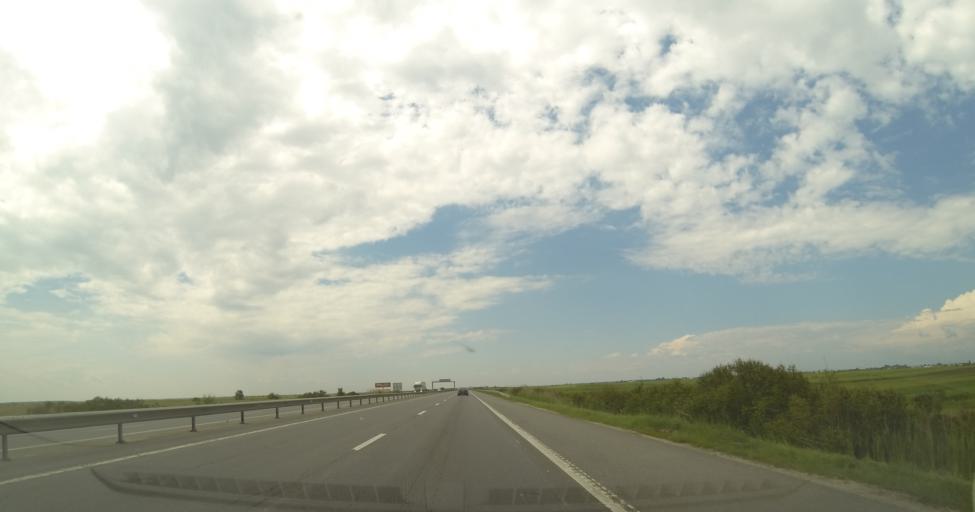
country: RO
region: Dambovita
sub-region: Comuna Petresti
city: Petresti
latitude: 44.6602
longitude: 25.3291
